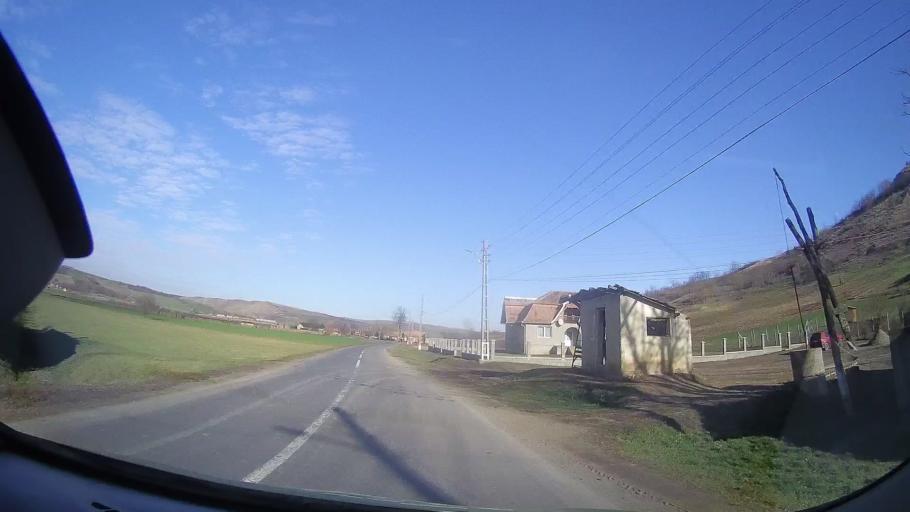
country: RO
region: Mures
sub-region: Comuna Iclanzel
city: Iclanzel
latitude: 46.5540
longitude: 24.3354
